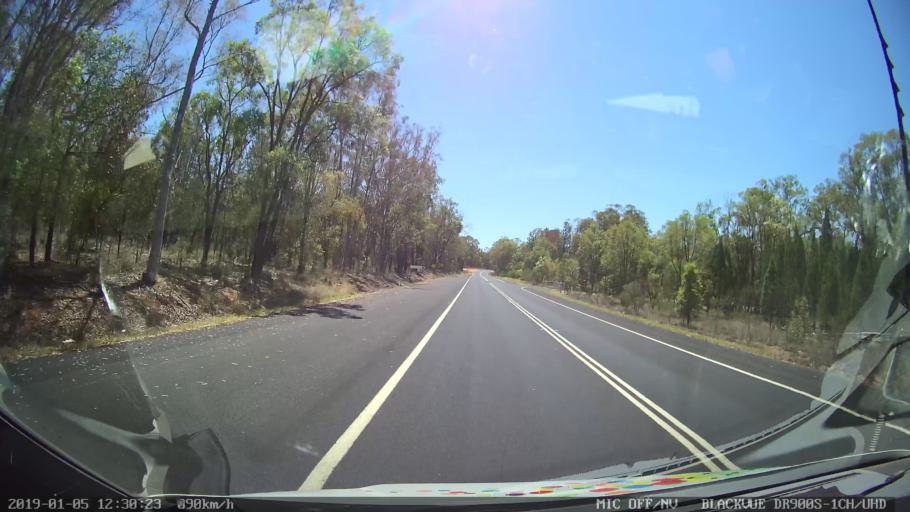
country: AU
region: New South Wales
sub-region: Warrumbungle Shire
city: Coonabarabran
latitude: -31.2282
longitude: 149.3498
